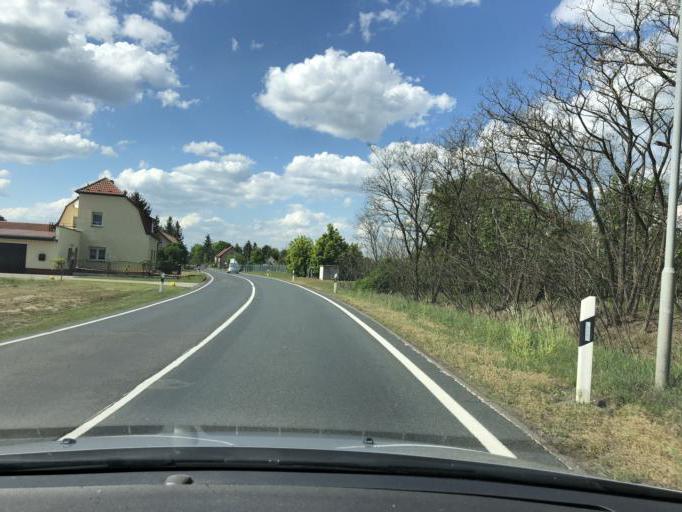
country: DE
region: Brandenburg
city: Spreenhagen
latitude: 52.3336
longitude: 13.8968
